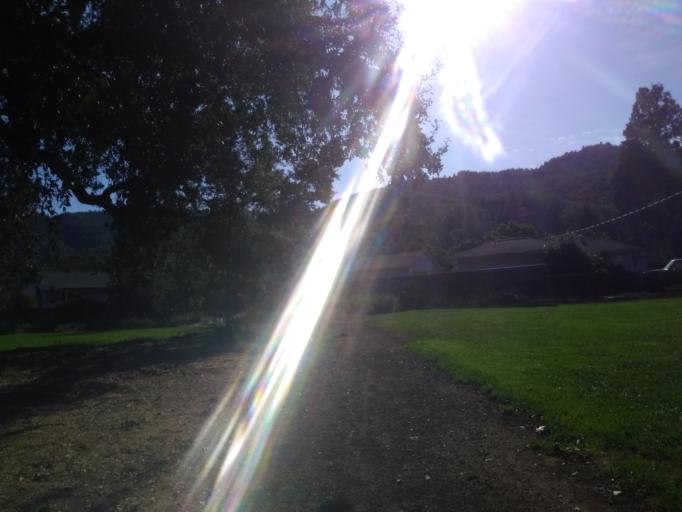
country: US
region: California
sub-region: Mendocino County
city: Ukiah
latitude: 39.1384
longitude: -123.2119
